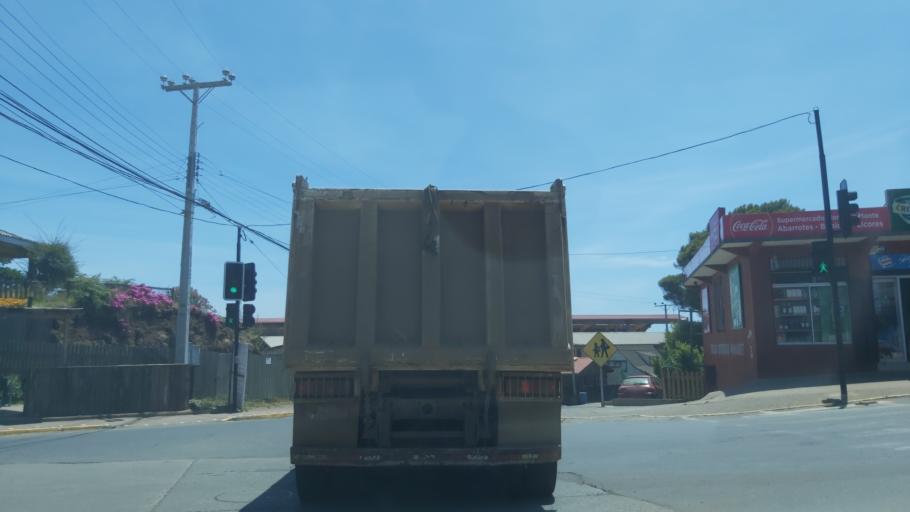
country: CL
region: Maule
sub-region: Provincia de Cauquenes
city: Cauquenes
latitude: -35.8137
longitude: -72.5735
